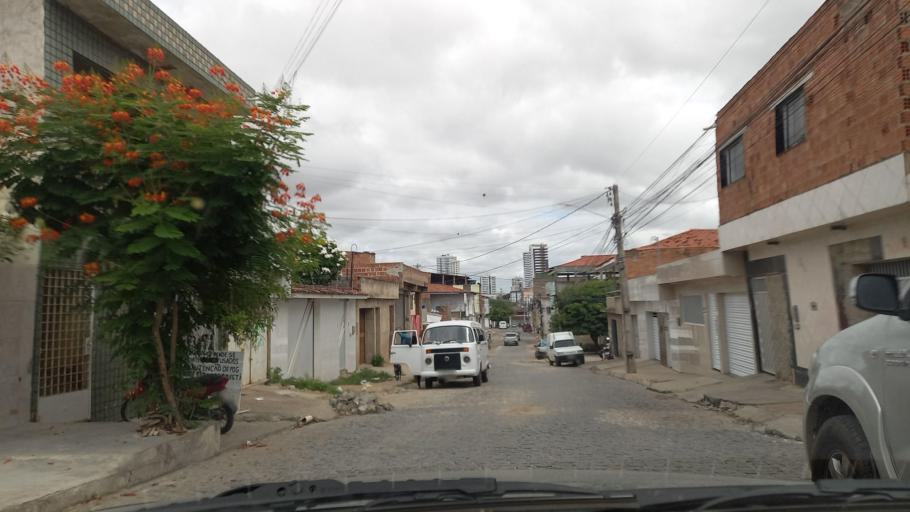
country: BR
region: Pernambuco
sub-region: Caruaru
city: Caruaru
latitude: -8.2702
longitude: -35.9570
